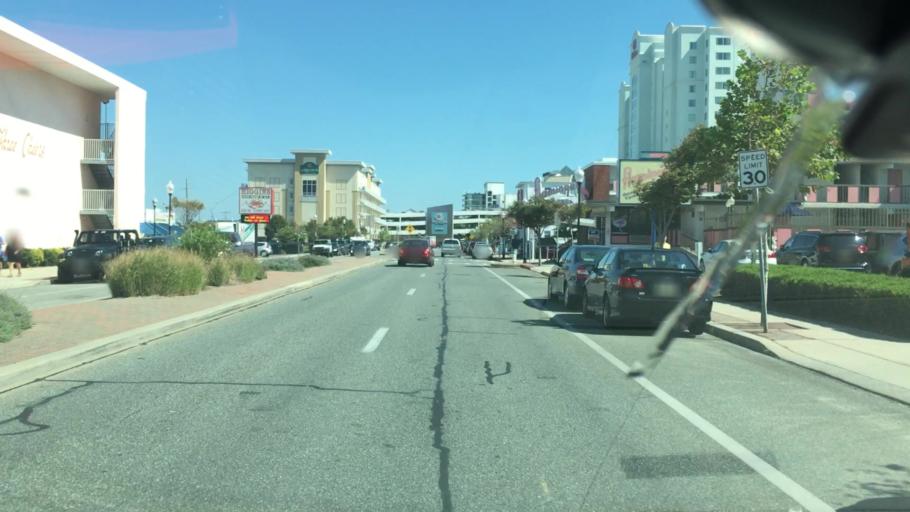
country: US
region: Maryland
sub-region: Worcester County
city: Ocean City
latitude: 38.3590
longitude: -75.0730
